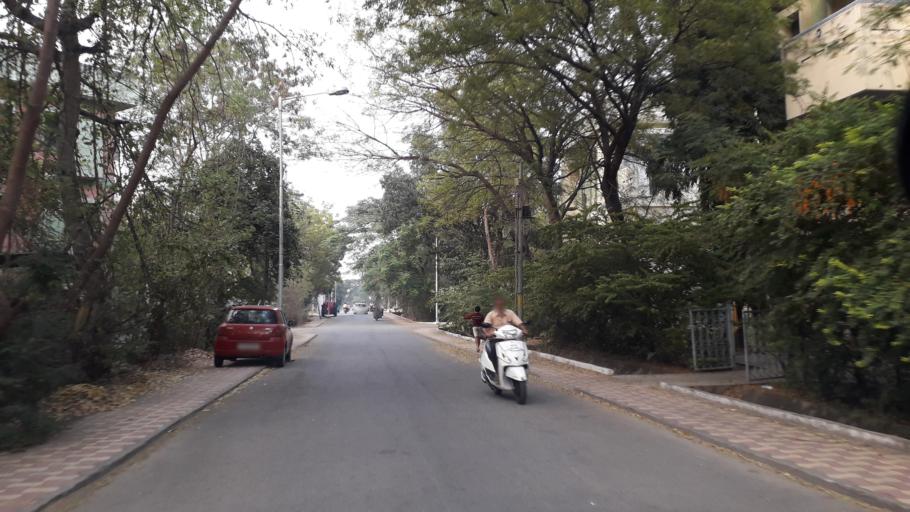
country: IN
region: Telangana
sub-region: Rangareddi
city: Singapur
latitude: 17.4677
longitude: 78.1630
